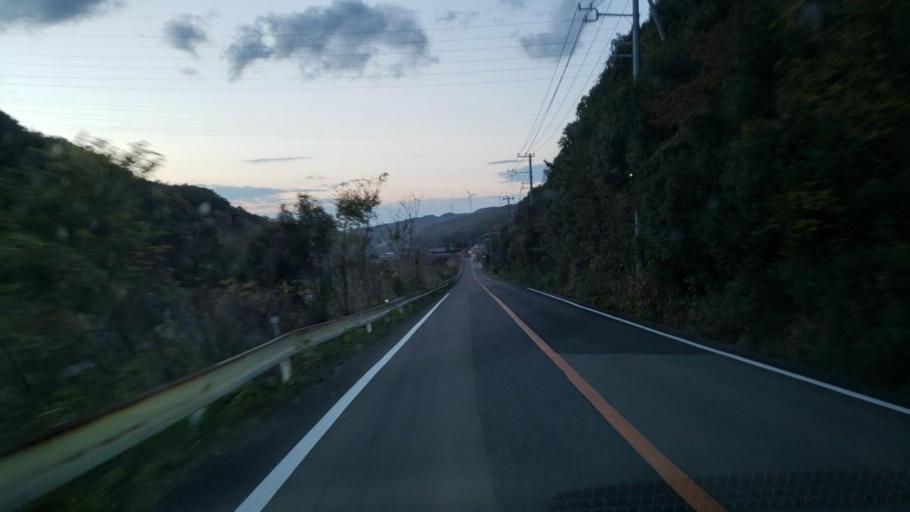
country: JP
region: Hyogo
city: Fukura
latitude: 34.2792
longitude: 134.7017
